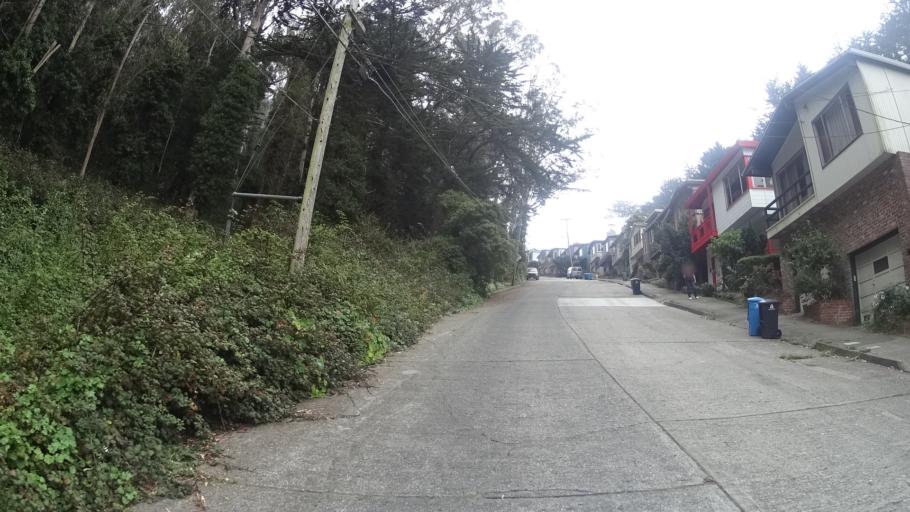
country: US
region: California
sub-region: San Mateo County
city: Daly City
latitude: 37.7382
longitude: -122.4569
